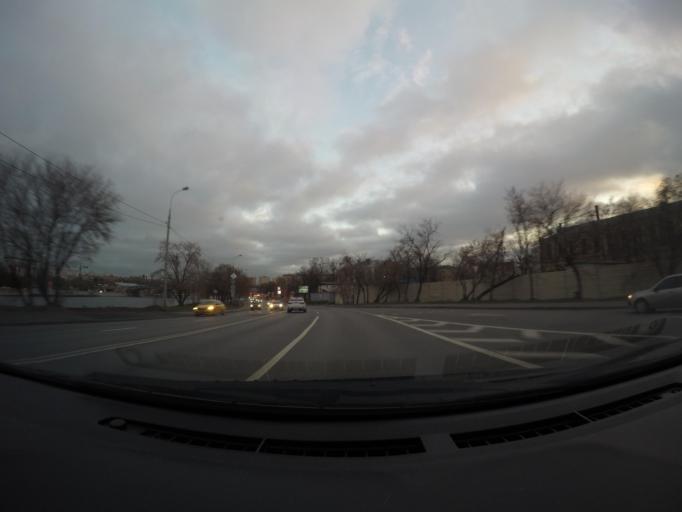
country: RU
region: Moscow
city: Zamoskvorech'ye
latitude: 55.7310
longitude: 37.6491
